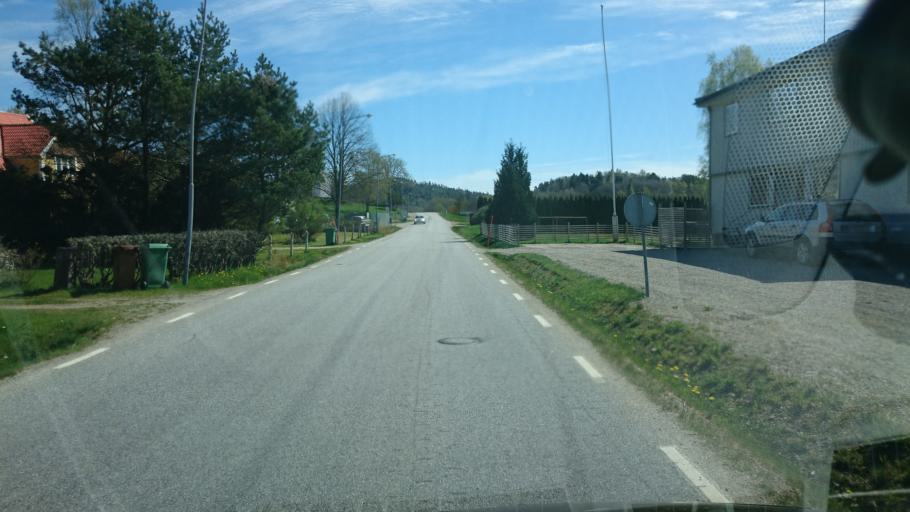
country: SE
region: Vaestra Goetaland
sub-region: Munkedals Kommun
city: Munkedal
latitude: 58.3805
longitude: 11.6671
